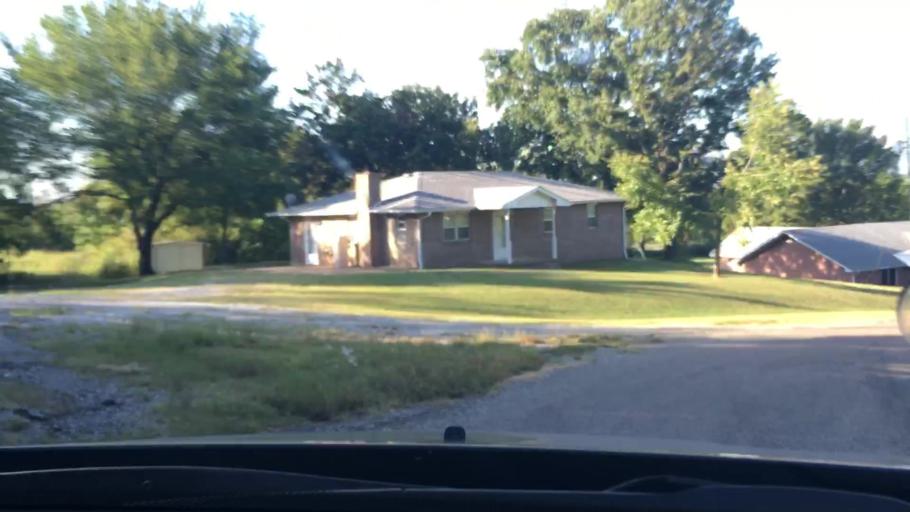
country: US
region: Oklahoma
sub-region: Pontotoc County
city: Ada
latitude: 34.7013
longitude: -96.4305
